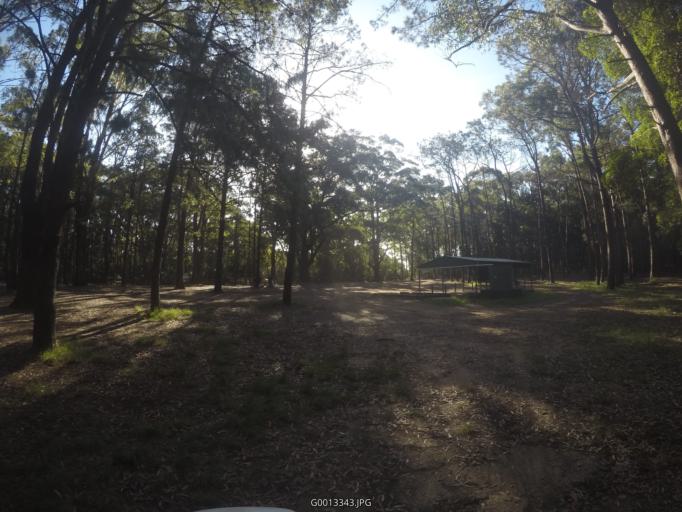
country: AU
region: New South Wales
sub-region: Lake Macquarie Shire
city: Cooranbong
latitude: -33.0625
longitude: 151.3322
